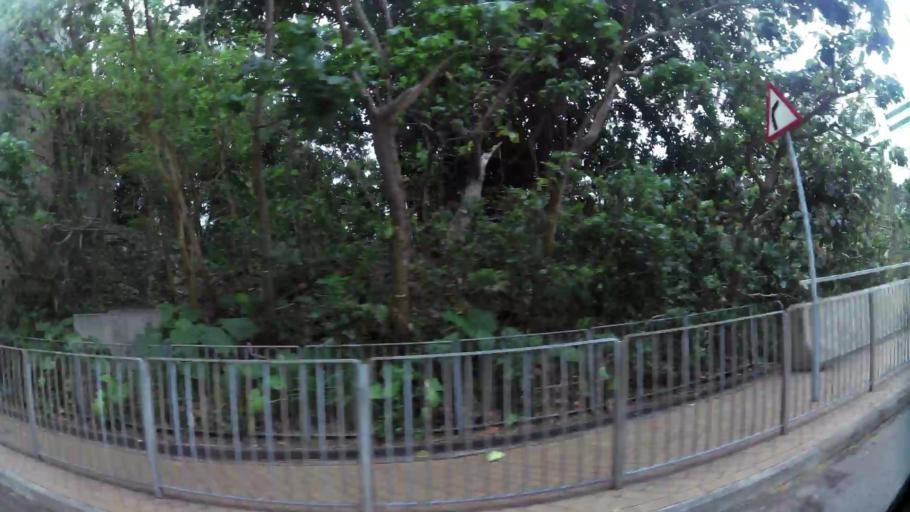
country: HK
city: Yung Shue Wan
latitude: 22.2539
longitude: 114.1338
